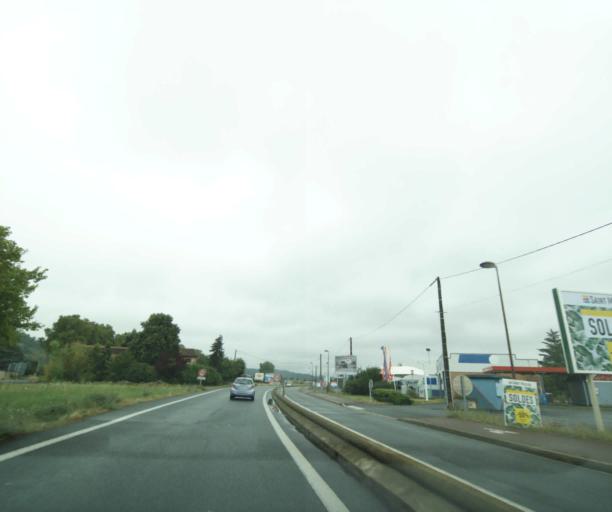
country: FR
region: Midi-Pyrenees
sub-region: Departement du Tarn
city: Albi
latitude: 43.9552
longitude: 2.1563
